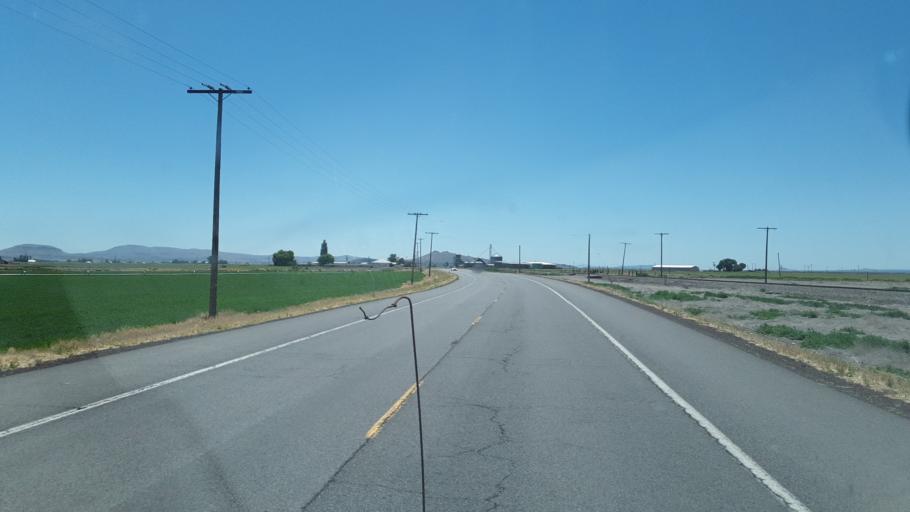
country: US
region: California
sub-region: Siskiyou County
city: Tulelake
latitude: 41.9491
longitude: -121.4647
